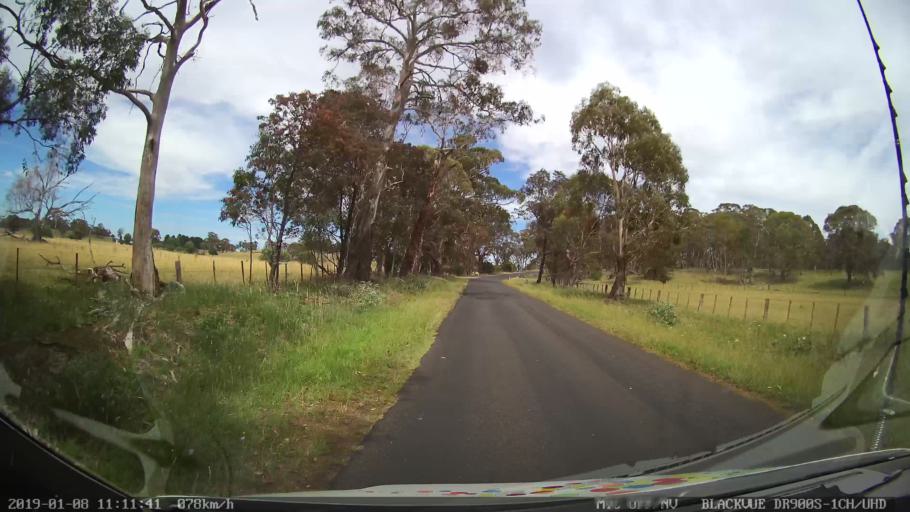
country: AU
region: New South Wales
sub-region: Guyra
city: Guyra
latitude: -30.2269
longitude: 151.6209
